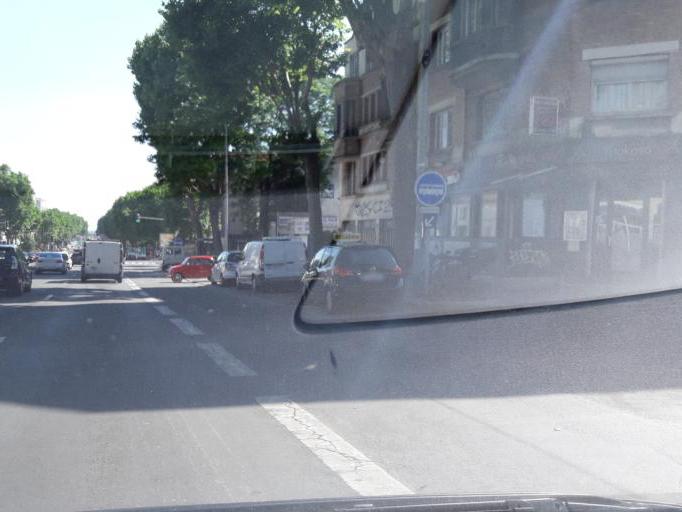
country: FR
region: Ile-de-France
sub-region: Departement du Val-de-Marne
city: Arcueil
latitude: 48.8028
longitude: 2.3244
